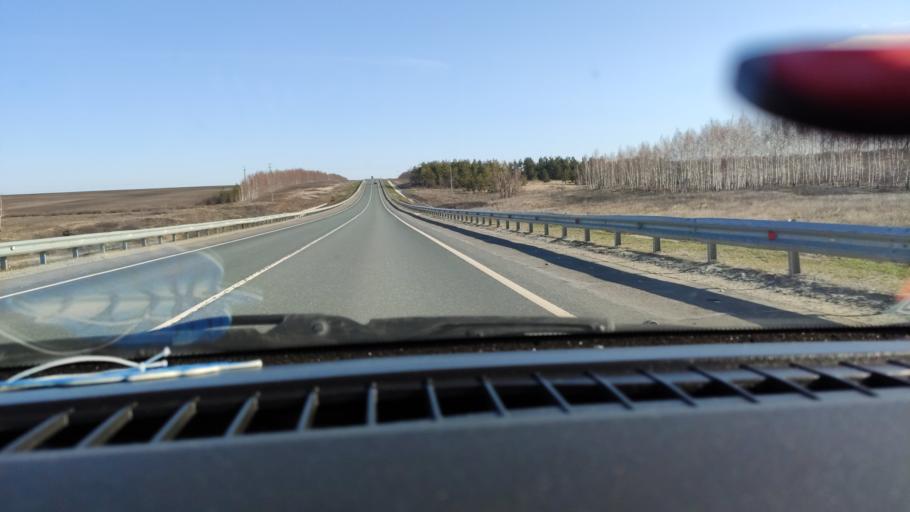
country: RU
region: Samara
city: Syzran'
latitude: 52.8999
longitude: 48.2966
